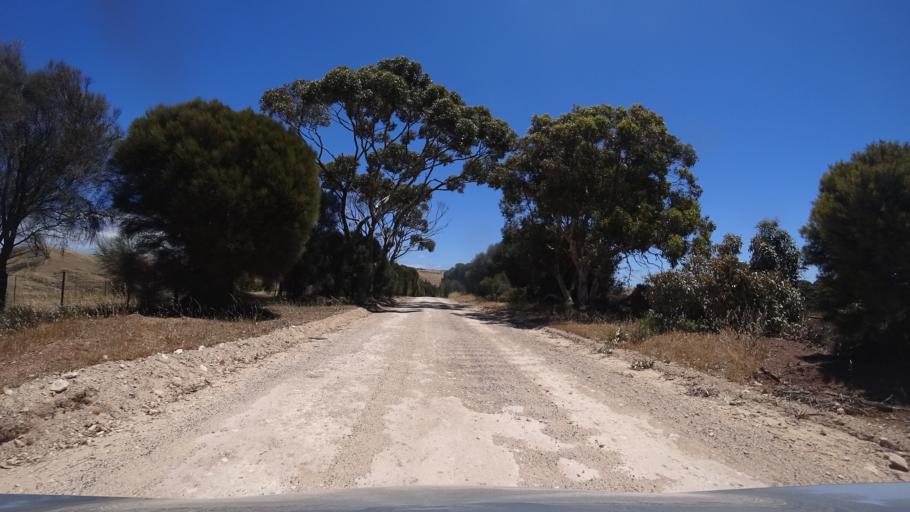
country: AU
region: South Australia
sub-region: Kangaroo Island
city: Kingscote
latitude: -35.6699
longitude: 137.0953
